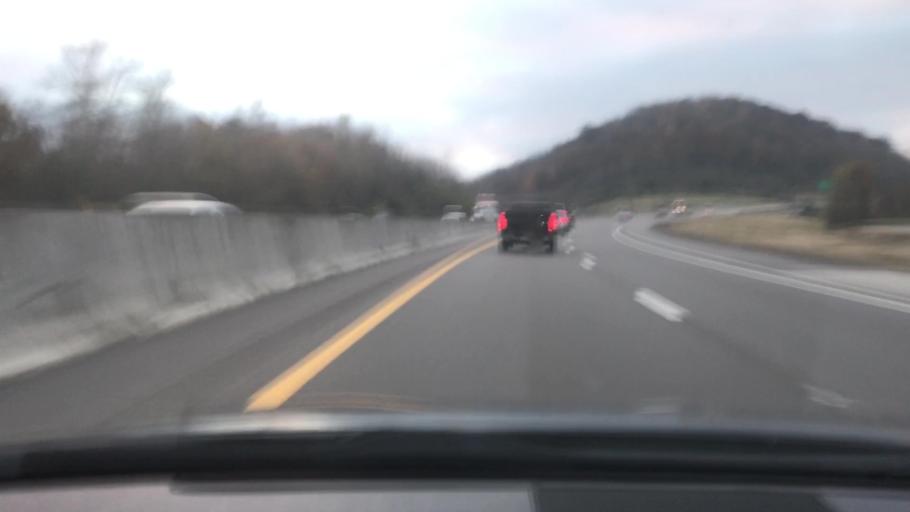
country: US
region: Tennessee
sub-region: Davidson County
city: Nashville
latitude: 36.2296
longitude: -86.8309
